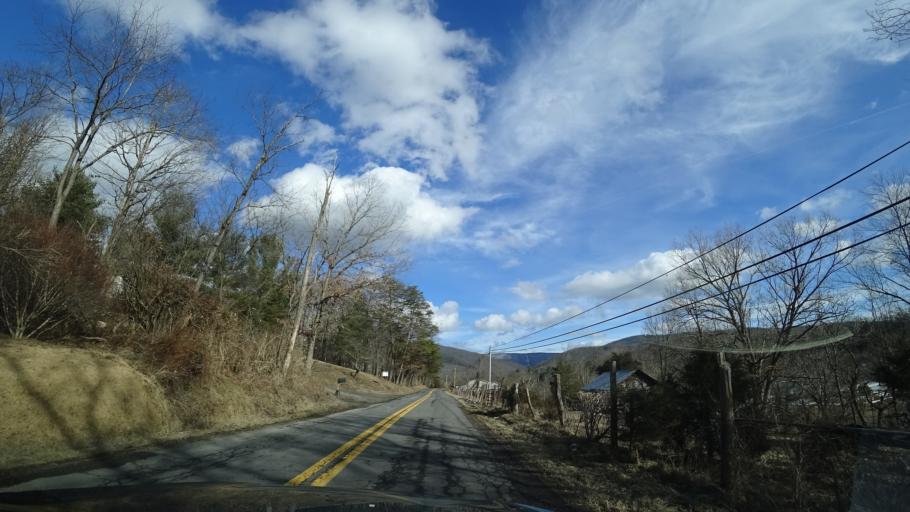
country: US
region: Virginia
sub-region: Shenandoah County
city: Basye
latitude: 38.8774
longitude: -78.8755
